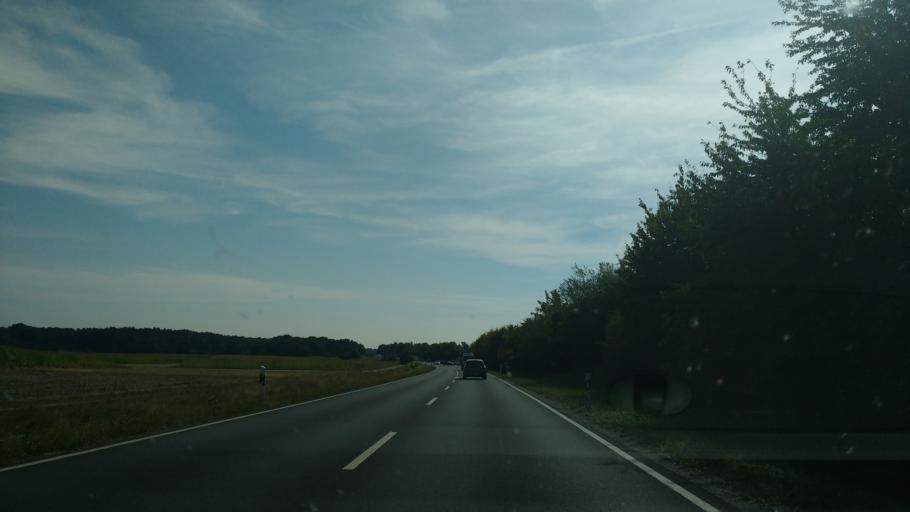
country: DE
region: Bavaria
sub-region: Regierungsbezirk Mittelfranken
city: Hessdorf
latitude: 49.6296
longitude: 10.9083
